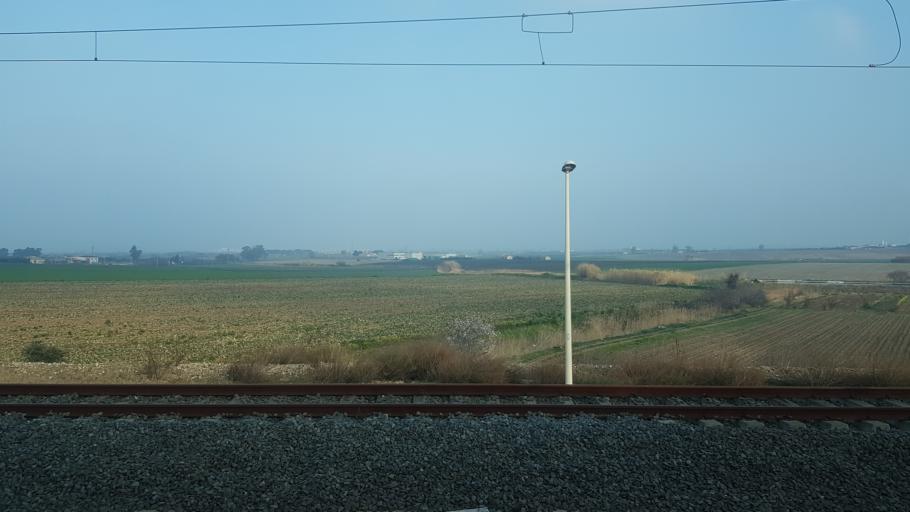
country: IT
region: Apulia
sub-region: Provincia di Foggia
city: Lesina
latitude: 41.8523
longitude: 15.2958
